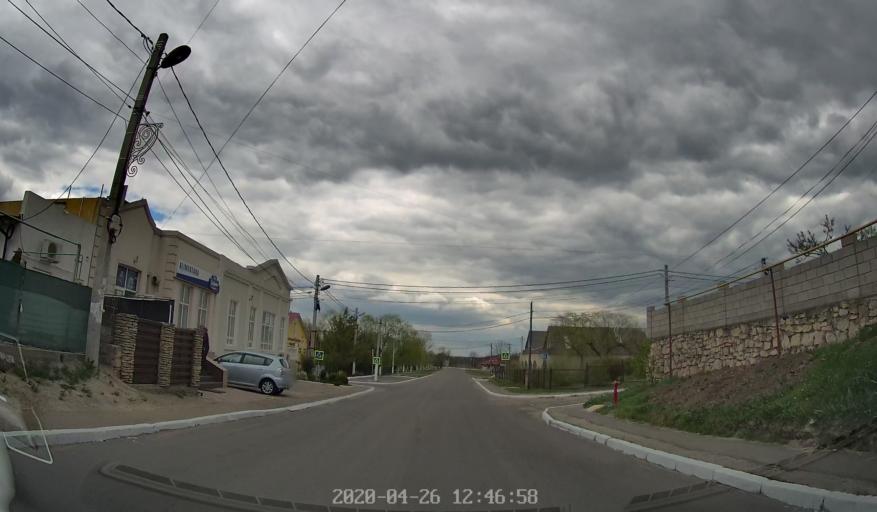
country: MD
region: Chisinau
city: Vadul lui Voda
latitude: 47.0627
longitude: 29.0010
